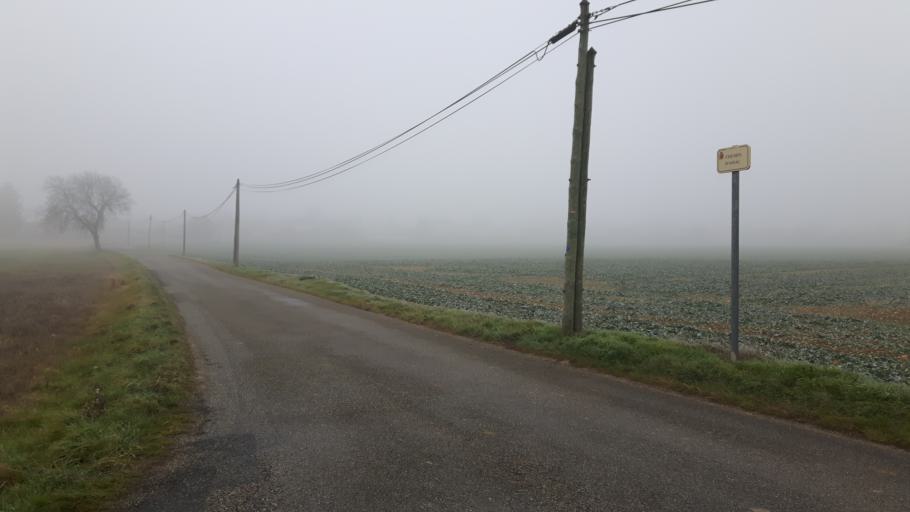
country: FR
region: Rhone-Alpes
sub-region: Departement de la Drome
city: Chabeuil
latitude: 44.8914
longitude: 5.0206
